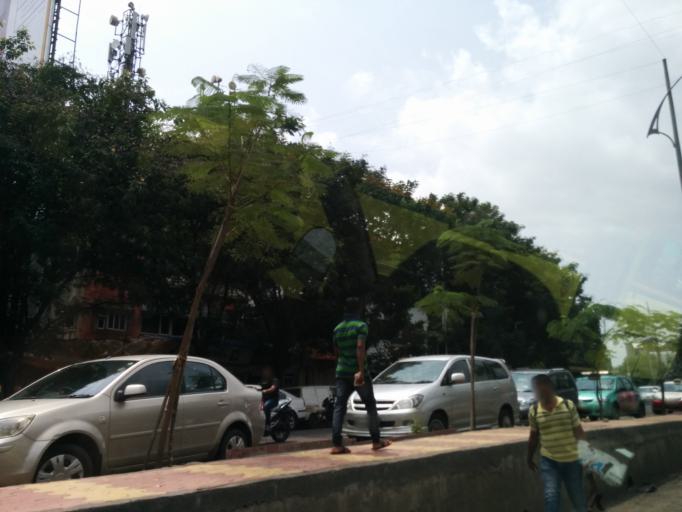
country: IN
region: Maharashtra
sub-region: Thane
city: Thane
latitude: 19.2132
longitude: 72.9772
